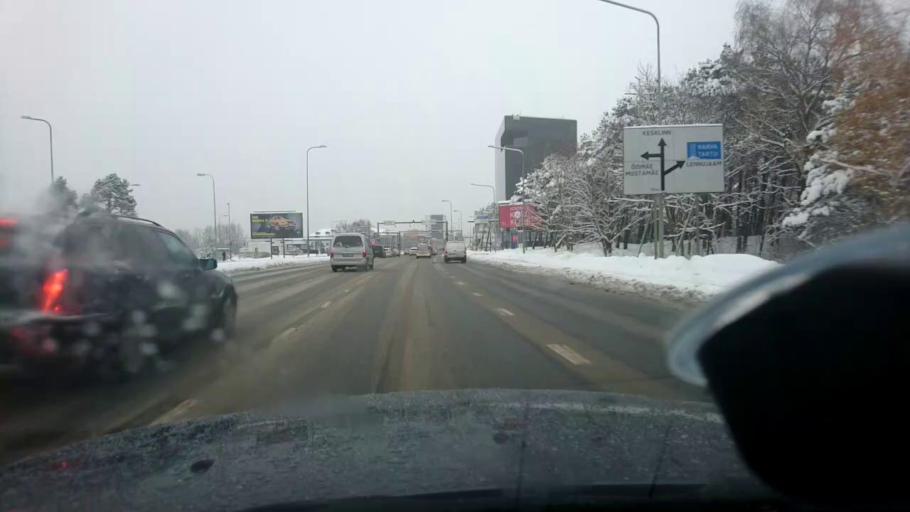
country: EE
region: Harju
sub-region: Tallinna linn
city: Tallinn
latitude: 59.4007
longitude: 24.7283
